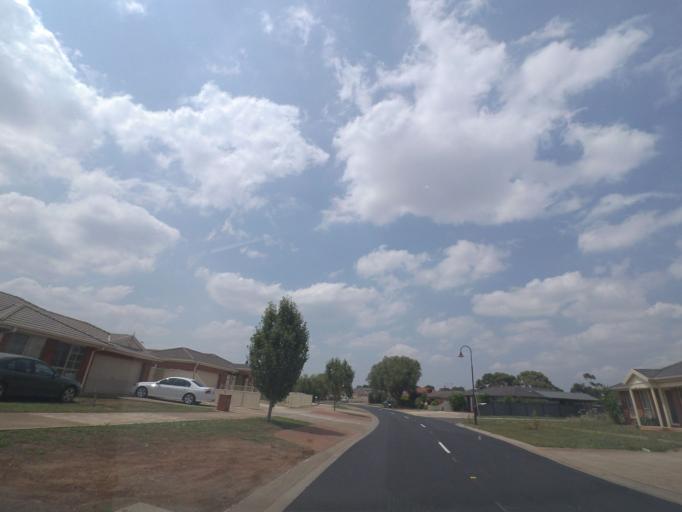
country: AU
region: Victoria
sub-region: Melton
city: Melton West
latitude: -37.6706
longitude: 144.5579
